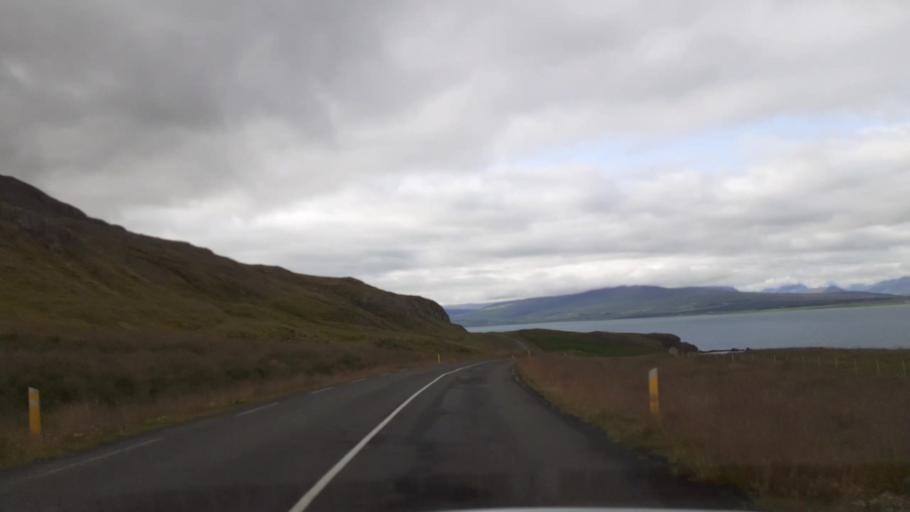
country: IS
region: Northeast
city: Akureyri
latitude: 65.8150
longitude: -18.0490
